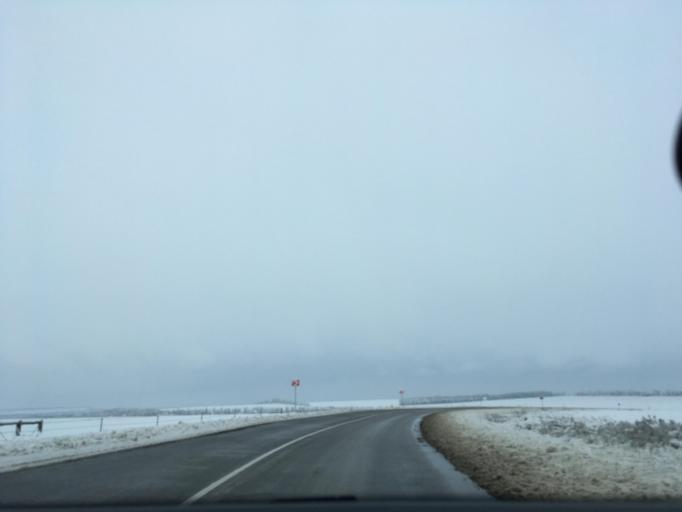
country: RU
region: Voronezj
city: Ol'khovatka
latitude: 50.2174
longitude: 39.2594
